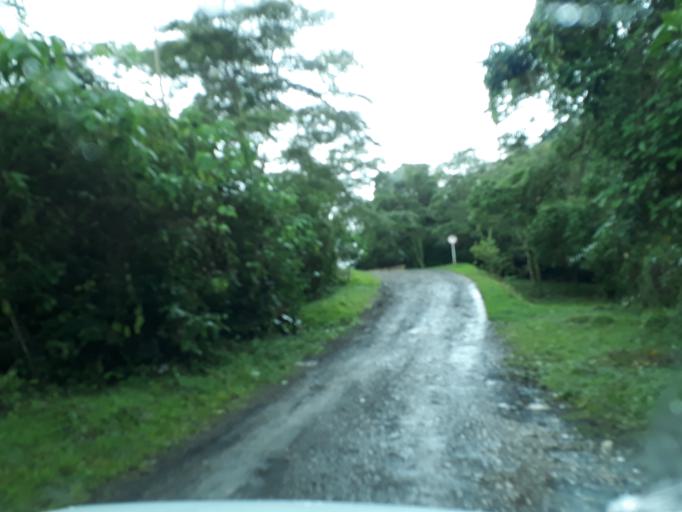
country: CO
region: Cundinamarca
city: Medina
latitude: 4.5868
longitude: -73.3775
